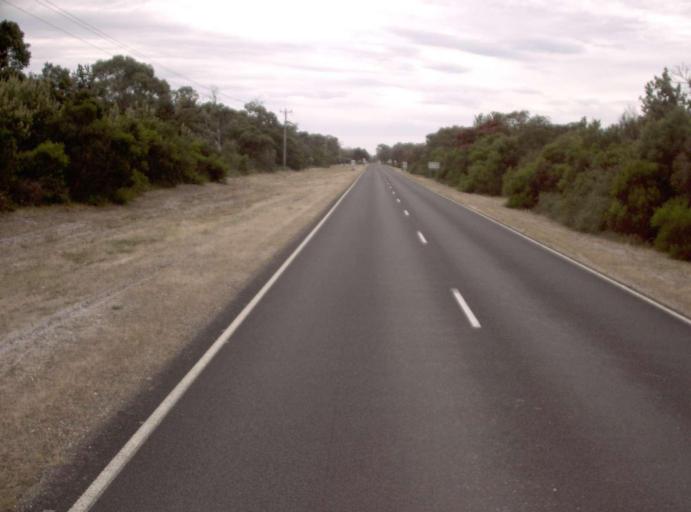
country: AU
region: Victoria
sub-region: East Gippsland
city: Bairnsdale
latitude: -38.0620
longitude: 147.5618
